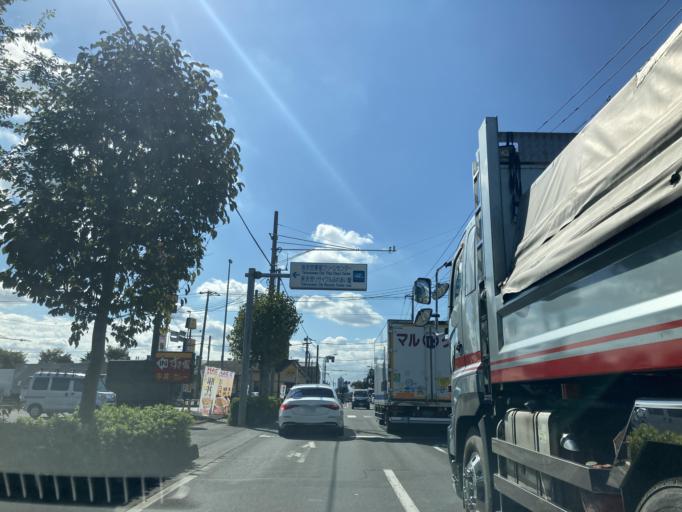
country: JP
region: Saitama
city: Tokorozawa
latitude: 35.8092
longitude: 139.4935
